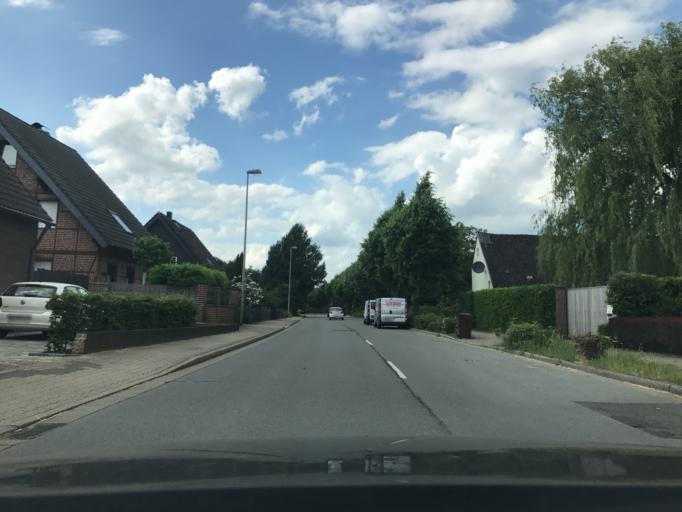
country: DE
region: North Rhine-Westphalia
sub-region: Regierungsbezirk Dusseldorf
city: Krefeld
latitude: 51.3168
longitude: 6.6292
